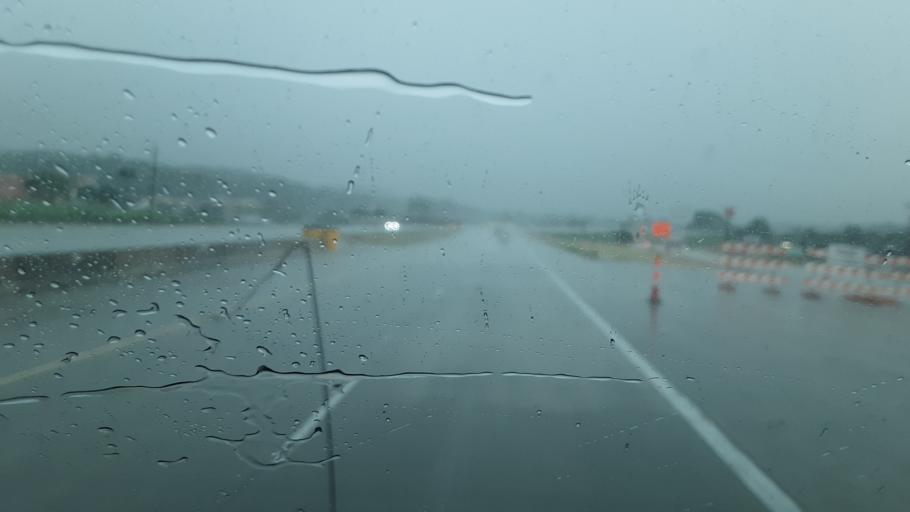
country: US
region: Iowa
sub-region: Pottawattamie County
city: Council Bluffs
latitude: 41.2383
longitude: -95.8255
